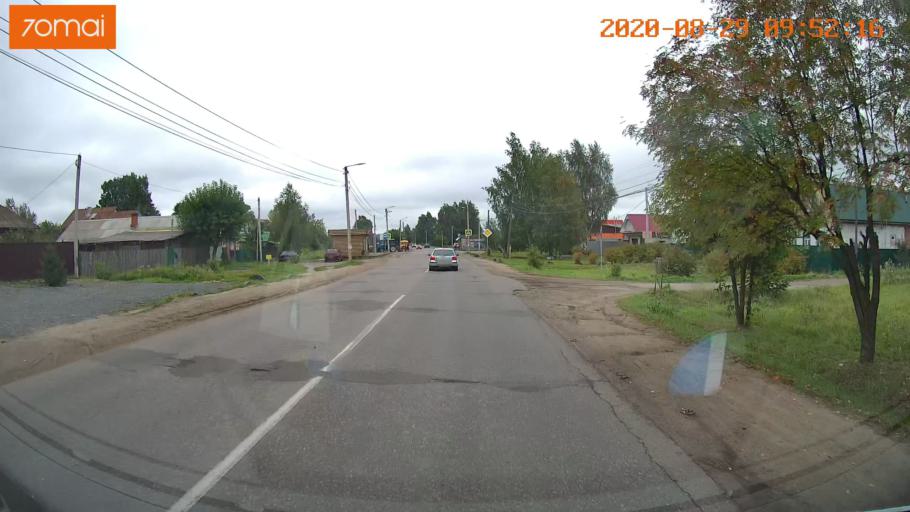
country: RU
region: Ivanovo
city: Kineshma
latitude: 57.4245
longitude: 42.2071
